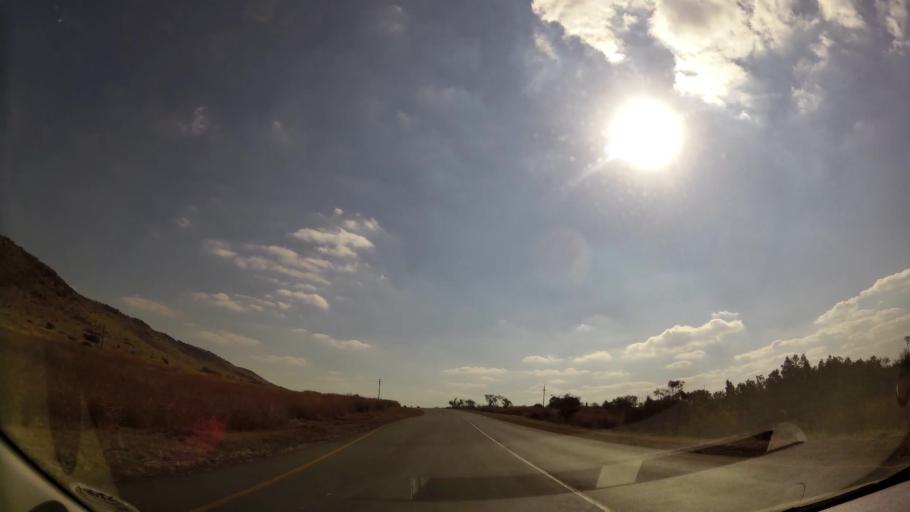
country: ZA
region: Gauteng
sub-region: West Rand District Municipality
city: Krugersdorp
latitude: -26.0395
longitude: 27.7731
